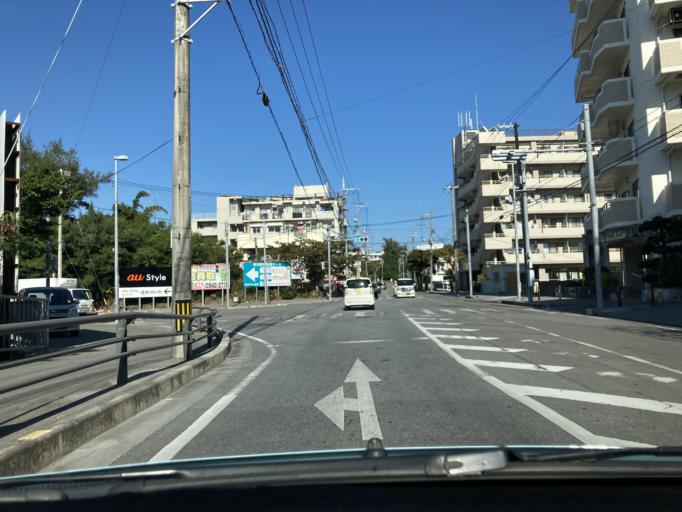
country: JP
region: Okinawa
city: Naha-shi
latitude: 26.2322
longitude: 127.7242
